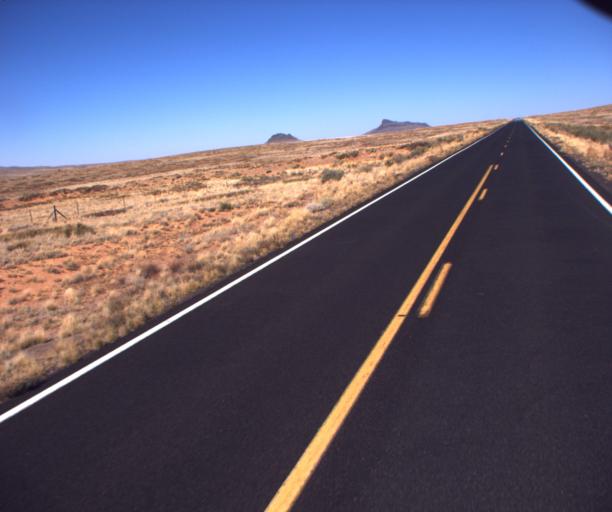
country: US
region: Arizona
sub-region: Navajo County
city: Dilkon
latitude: 35.3958
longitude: -110.4260
